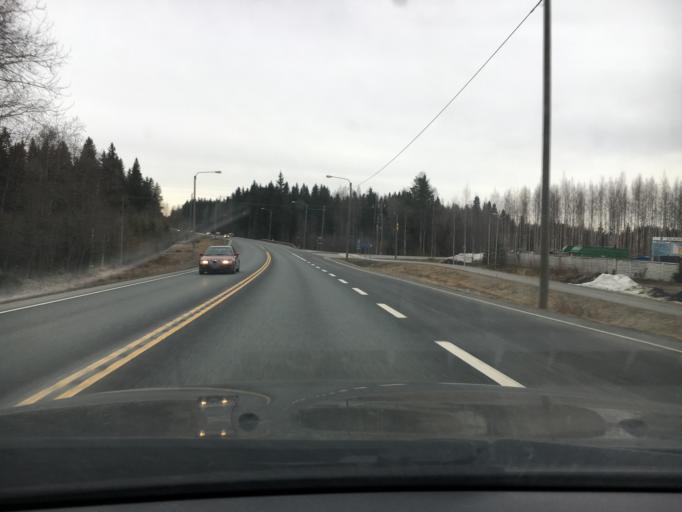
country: FI
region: Northern Savo
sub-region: Kuopio
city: Siilinjaervi
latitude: 63.0929
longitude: 27.6522
